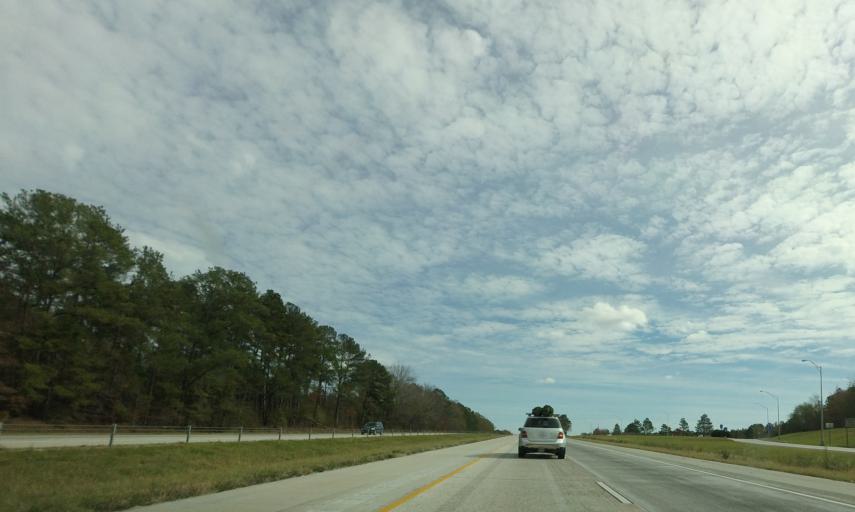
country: US
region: Georgia
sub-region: Laurens County
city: Dublin
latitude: 32.5093
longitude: -83.0512
